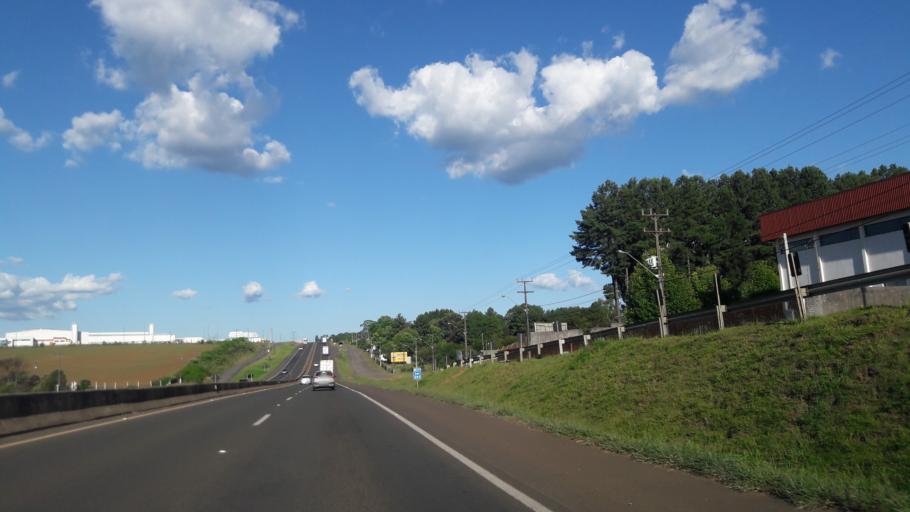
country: BR
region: Parana
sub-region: Guarapuava
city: Guarapuava
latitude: -25.3481
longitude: -51.4536
